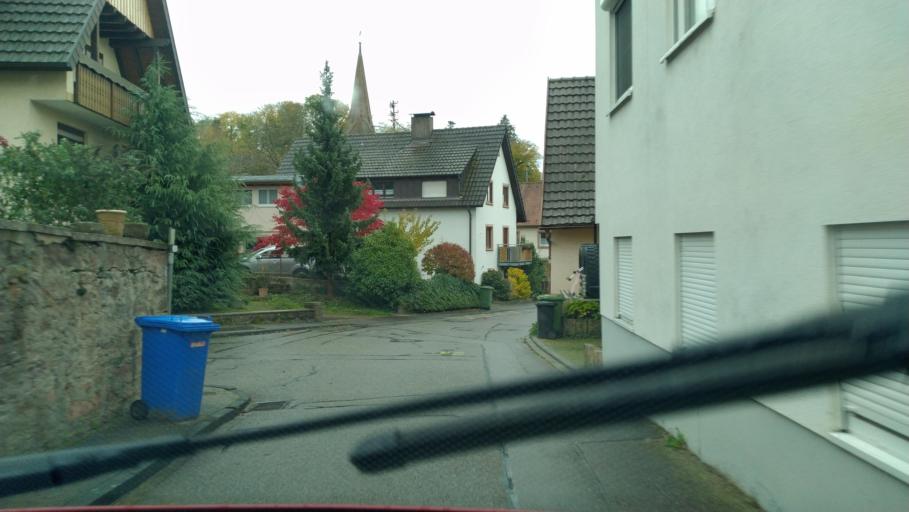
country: DE
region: Baden-Wuerttemberg
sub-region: Freiburg Region
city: Malterdingen
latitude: 48.1645
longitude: 7.8326
